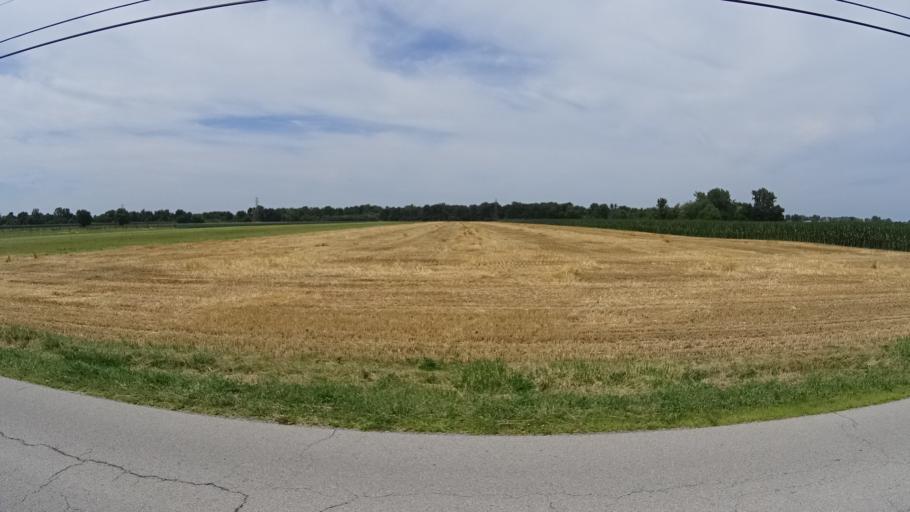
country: US
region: Ohio
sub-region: Erie County
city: Sandusky
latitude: 41.4276
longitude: -82.7546
